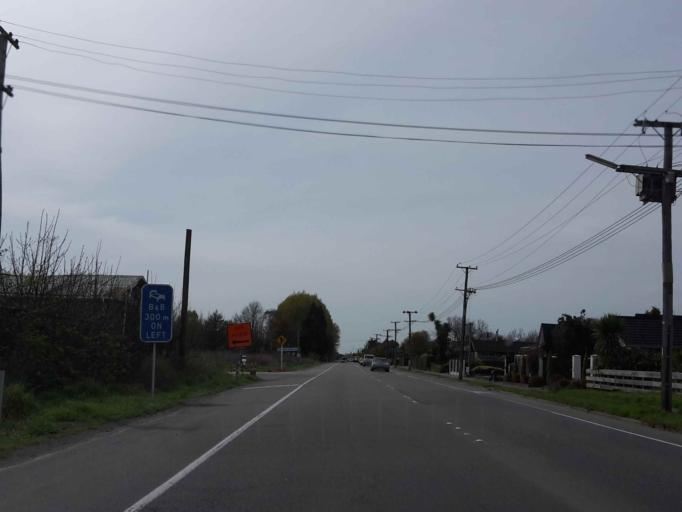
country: NZ
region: Canterbury
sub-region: Waimakariri District
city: Kaiapoi
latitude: -43.4521
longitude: 172.6160
